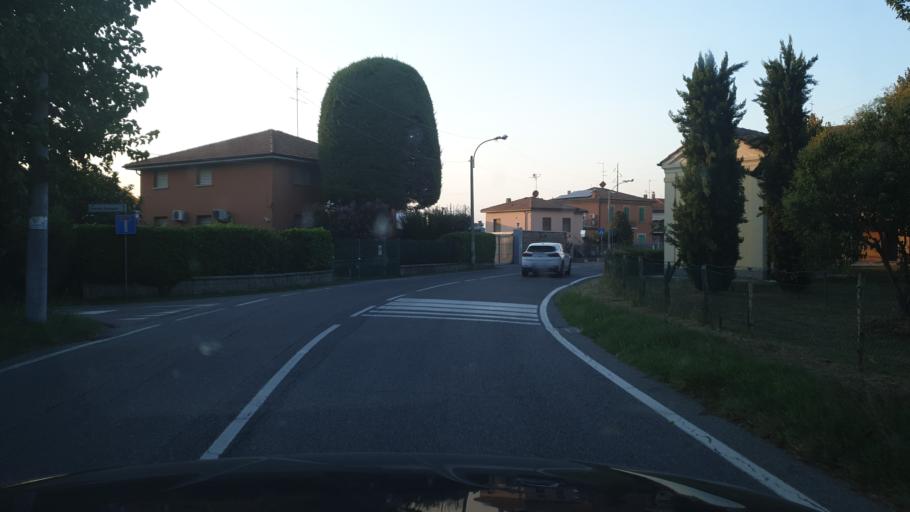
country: IT
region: Emilia-Romagna
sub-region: Provincia di Bologna
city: Quarto Inferiore
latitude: 44.5188
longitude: 11.3813
